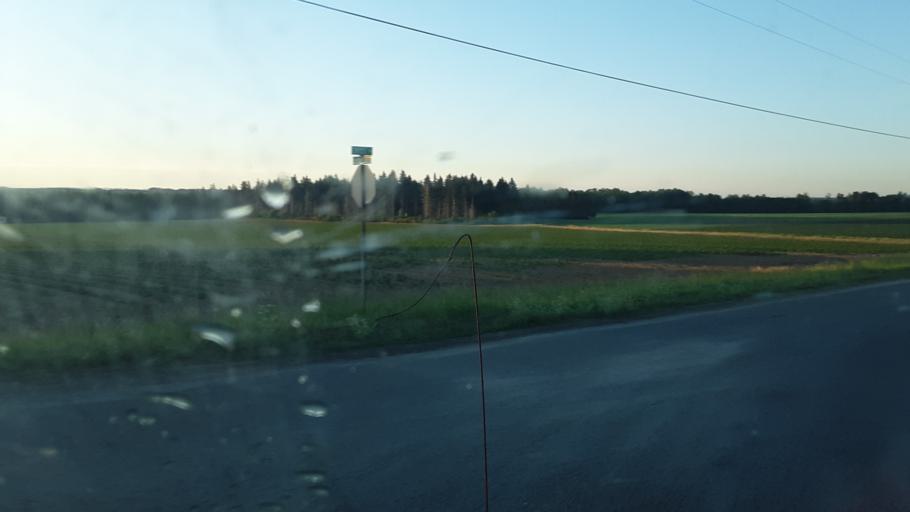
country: US
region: Maine
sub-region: Aroostook County
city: Caribou
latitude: 46.8028
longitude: -68.0980
